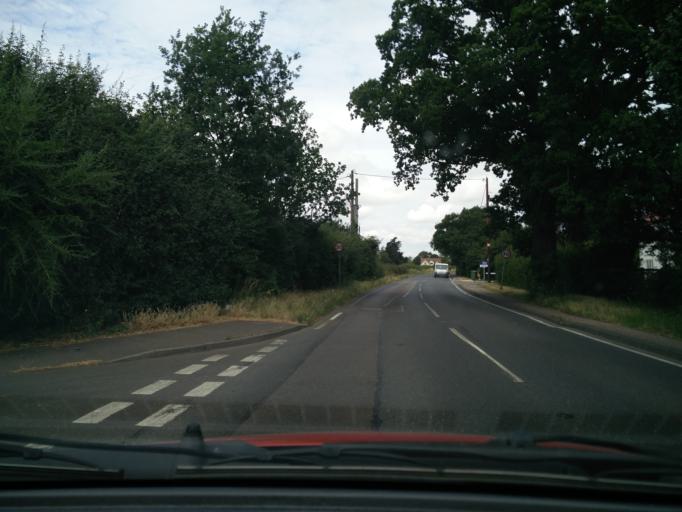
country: GB
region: England
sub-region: Essex
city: Burnham on Crouch
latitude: 51.6381
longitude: 0.8031
